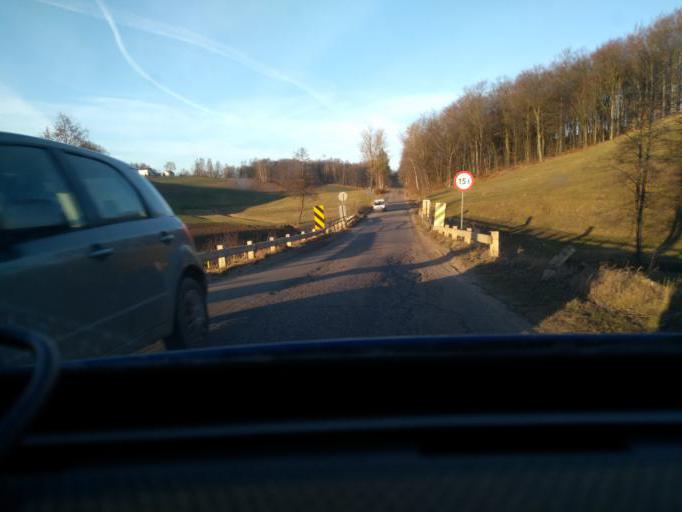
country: PL
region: Pomeranian Voivodeship
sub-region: Powiat kartuski
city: Przodkowo
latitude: 54.4051
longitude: 18.2925
